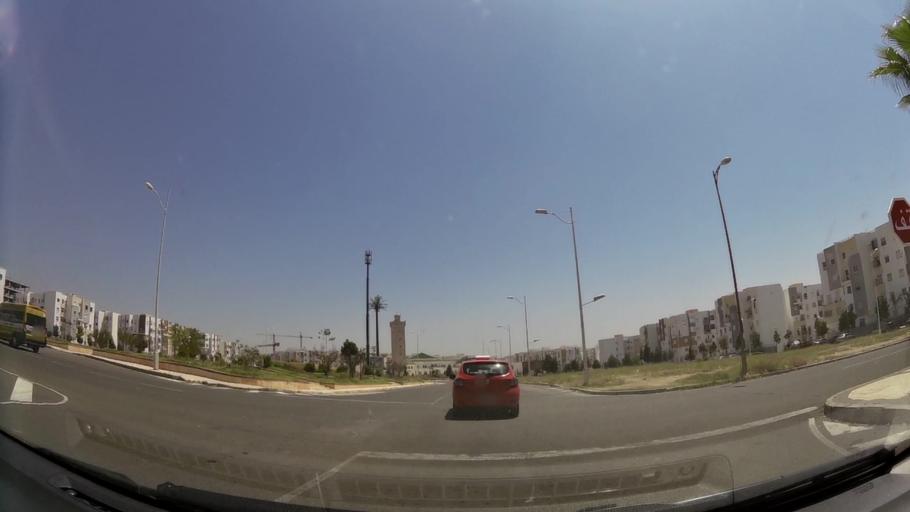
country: MA
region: Oued ed Dahab-Lagouira
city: Dakhla
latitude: 30.4347
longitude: -9.5588
